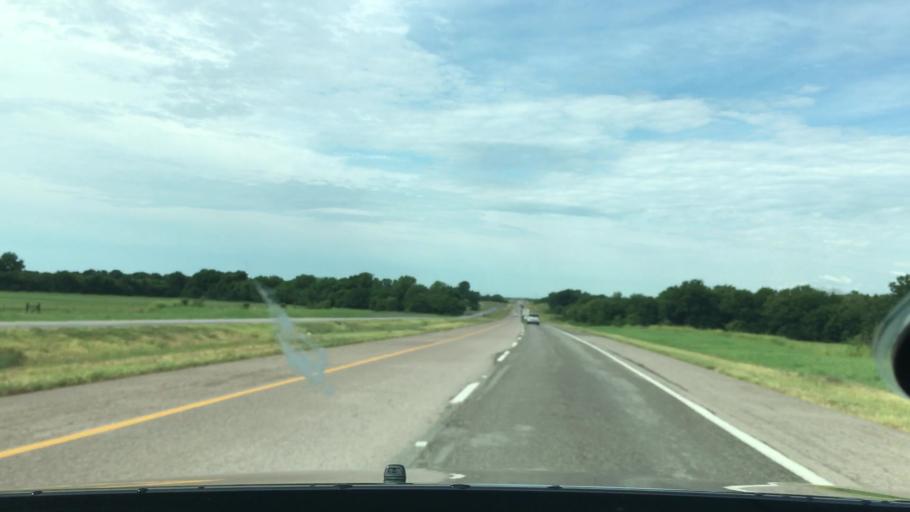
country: US
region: Oklahoma
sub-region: Pontotoc County
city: Ada
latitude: 34.6710
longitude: -96.7810
